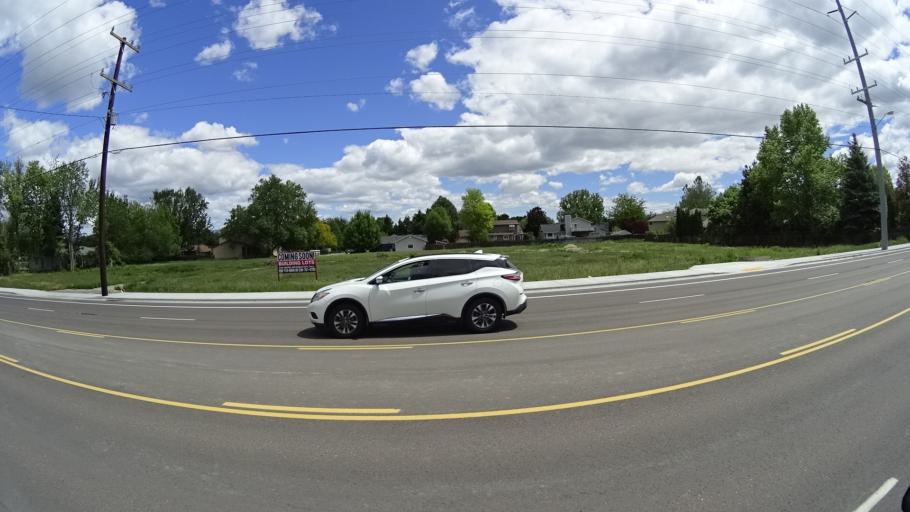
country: US
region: Idaho
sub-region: Ada County
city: Eagle
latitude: 43.6406
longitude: -116.3345
